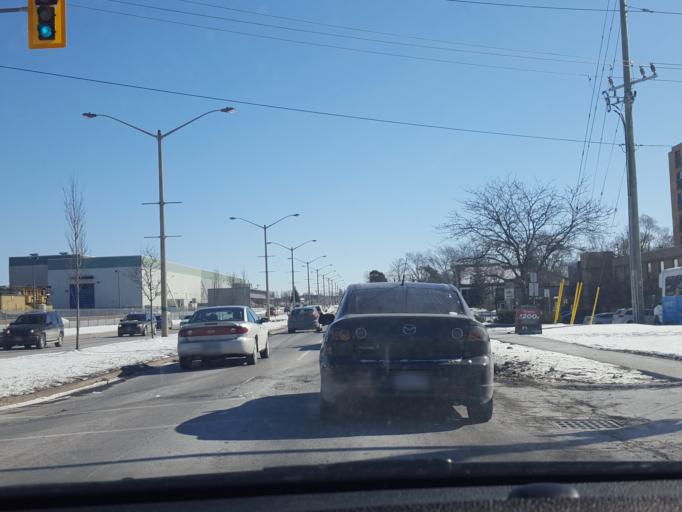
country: CA
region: Ontario
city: Cambridge
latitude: 43.3779
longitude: -80.3264
